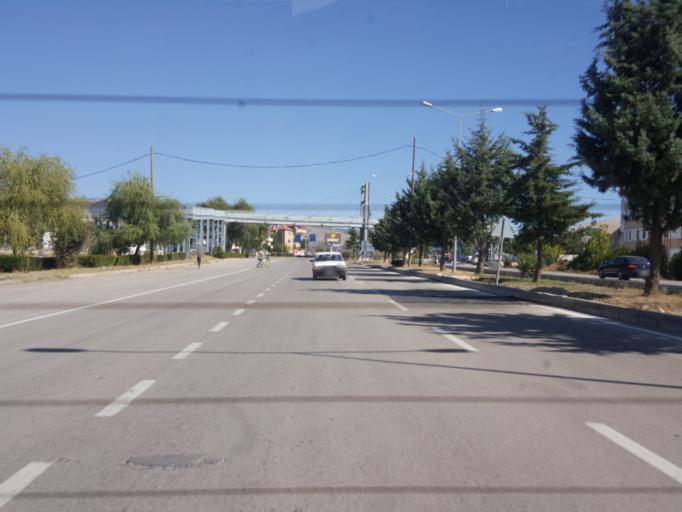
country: TR
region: Tokat
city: Zile
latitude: 40.3068
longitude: 35.9007
